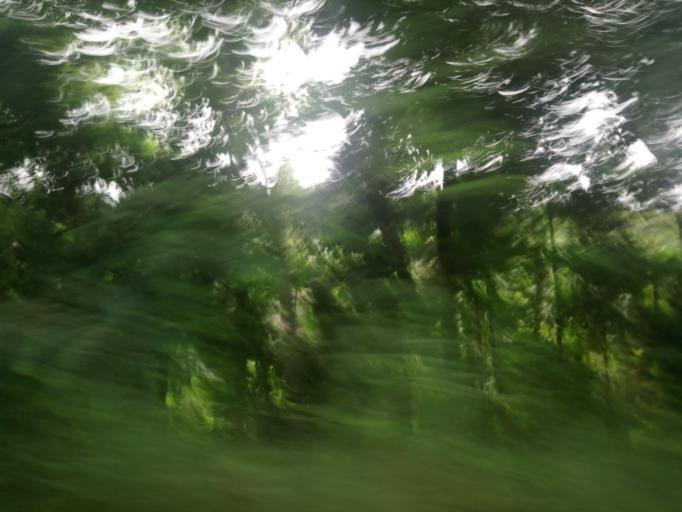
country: CM
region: Centre
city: Mbankomo
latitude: 3.7806
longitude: 11.0741
